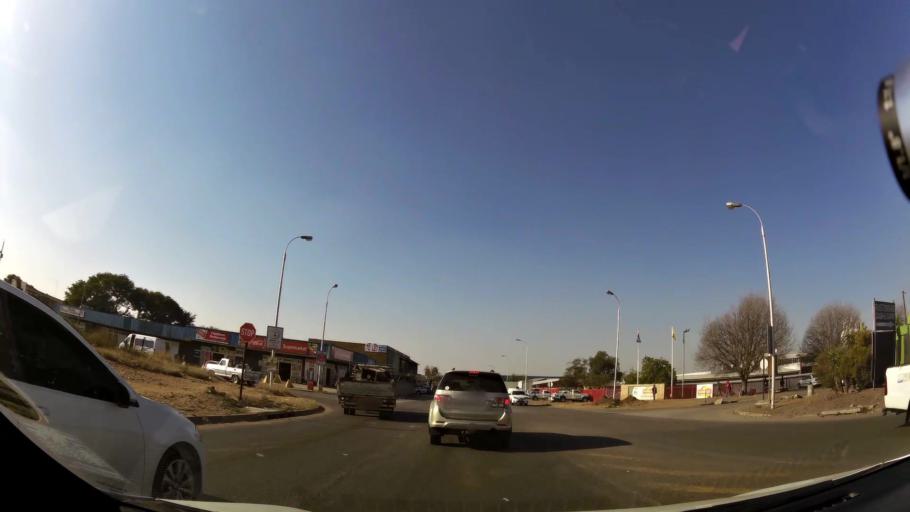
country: ZA
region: North-West
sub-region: Bojanala Platinum District Municipality
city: Rustenburg
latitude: -25.6684
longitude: 27.2577
